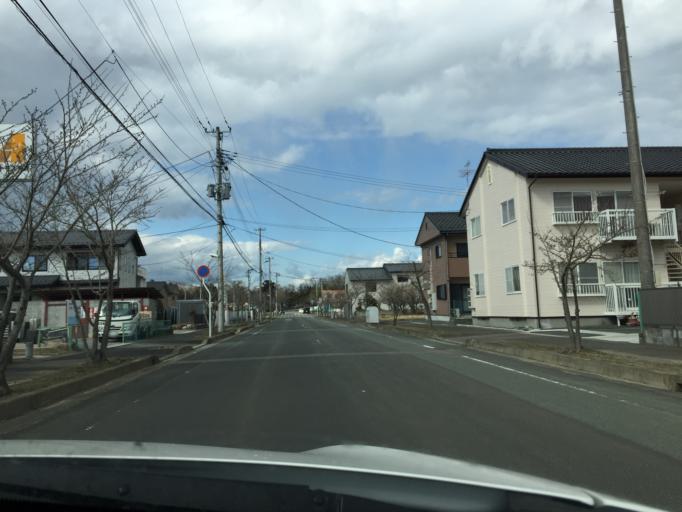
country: JP
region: Miyagi
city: Marumori
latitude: 37.8047
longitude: 140.9369
